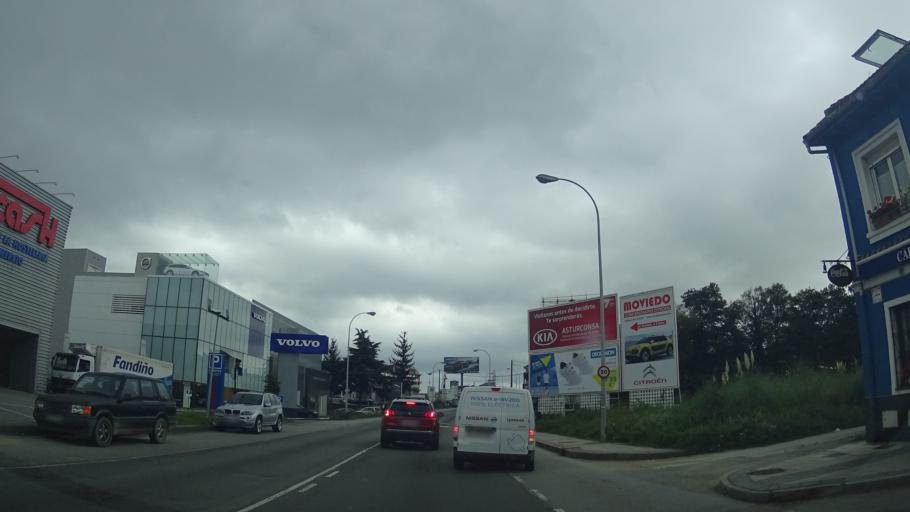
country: ES
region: Asturias
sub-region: Province of Asturias
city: Oviedo
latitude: 43.3699
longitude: -5.8181
